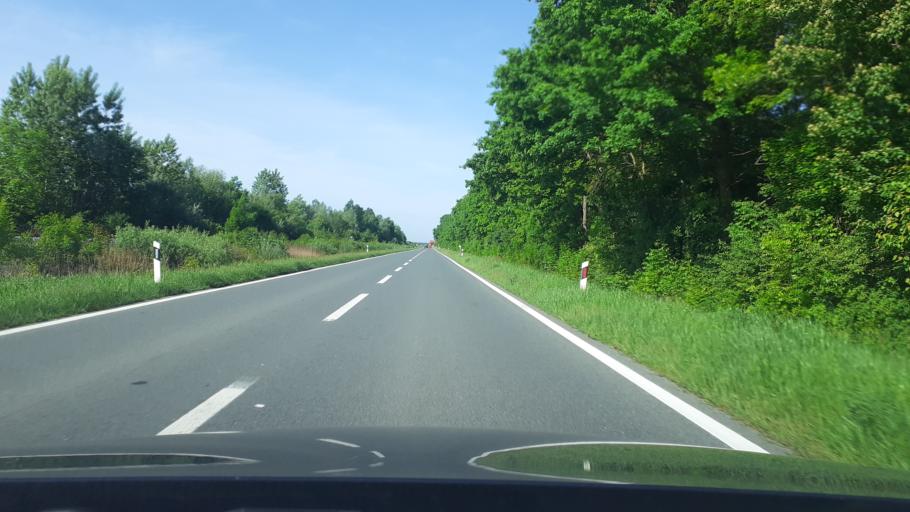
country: HR
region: Brodsko-Posavska
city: Oriovac
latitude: 45.2383
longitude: 17.7432
